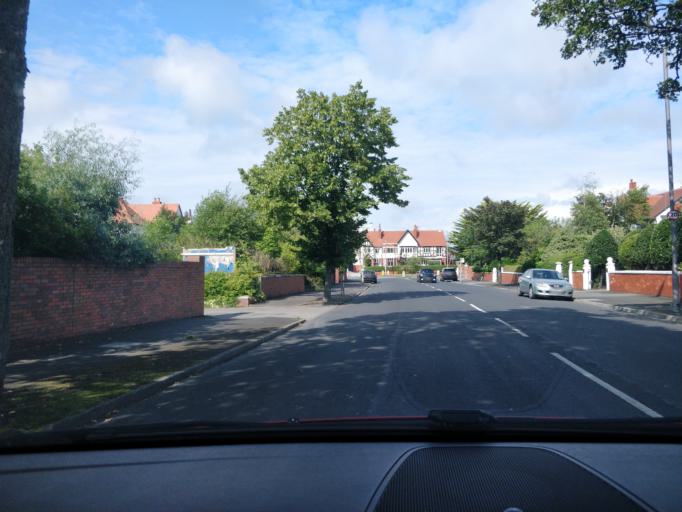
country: GB
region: England
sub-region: Sefton
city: Southport
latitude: 53.6595
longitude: -2.9857
